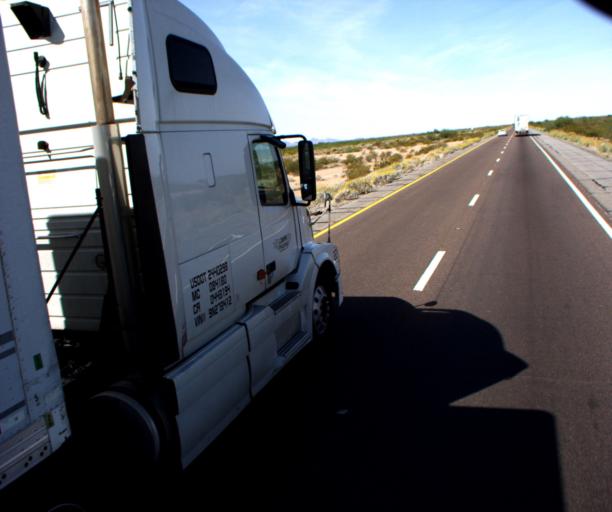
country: US
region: Arizona
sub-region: La Paz County
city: Salome
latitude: 33.5467
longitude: -113.2046
